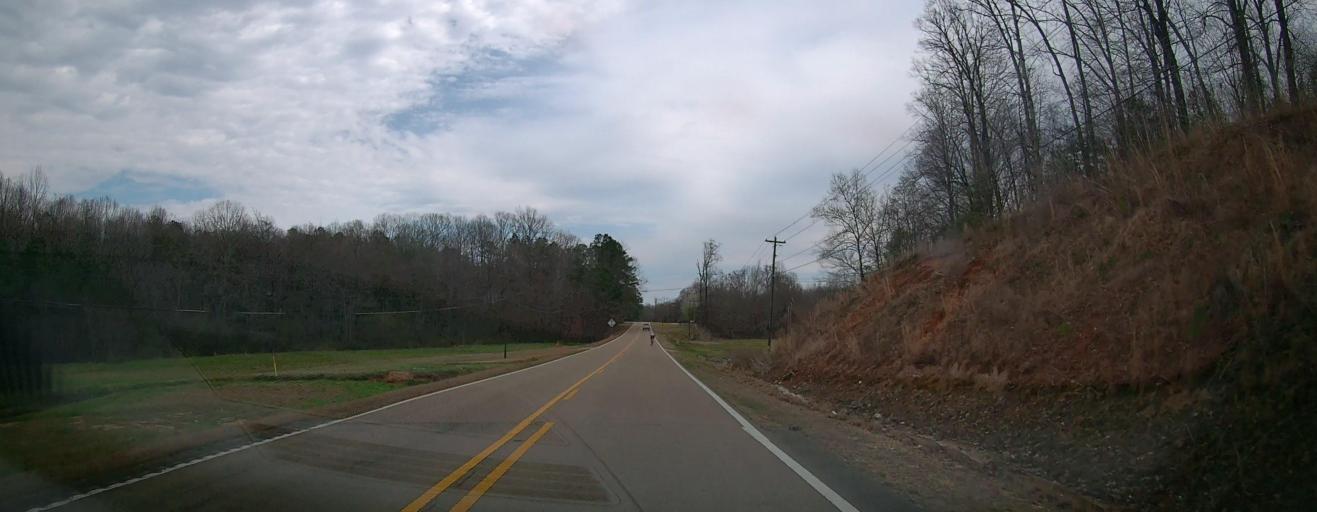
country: US
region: Mississippi
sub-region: Itawamba County
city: Fulton
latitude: 34.2627
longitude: -88.3256
